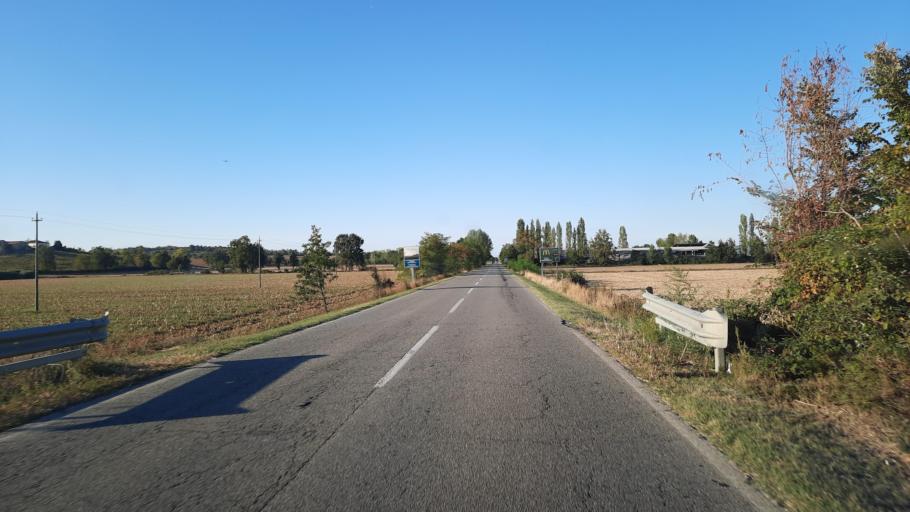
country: IT
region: Piedmont
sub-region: Provincia di Alessandria
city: Terruggia
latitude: 45.0736
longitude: 8.4682
